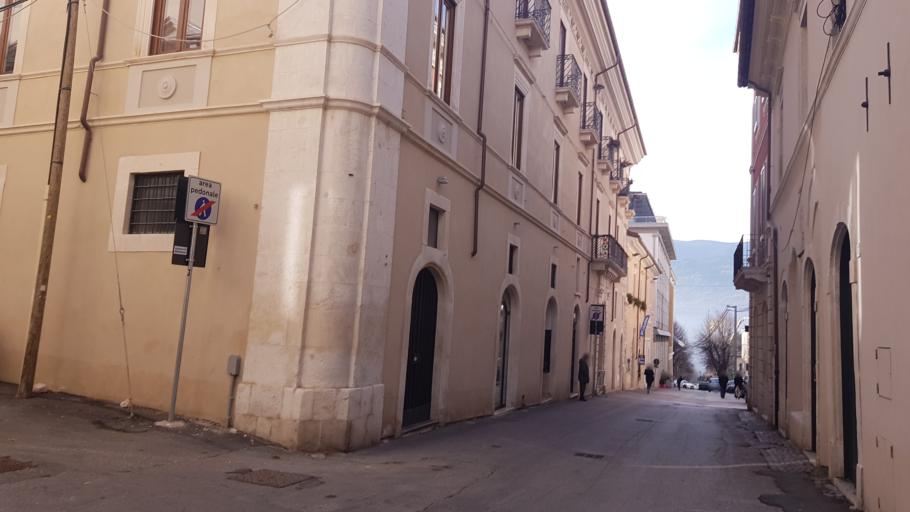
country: IT
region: Abruzzo
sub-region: Provincia dell' Aquila
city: L'Aquila
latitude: 42.3476
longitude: 13.3983
